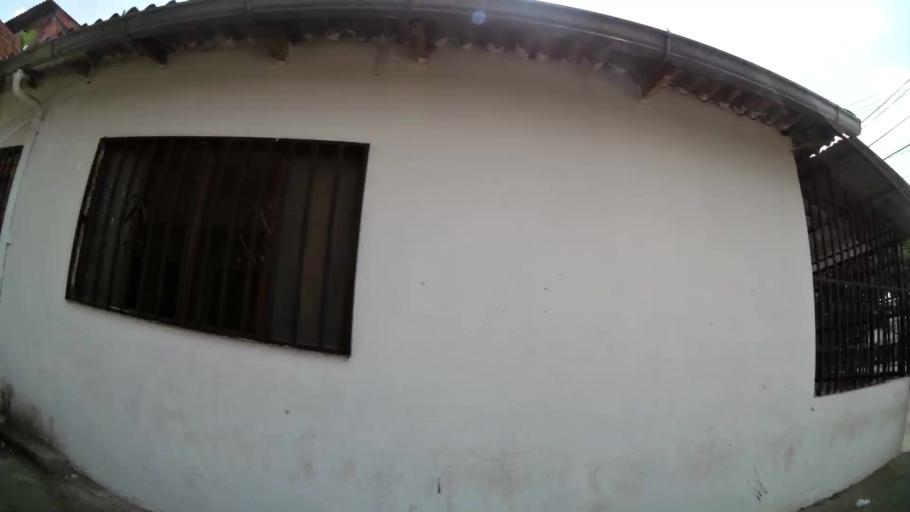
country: CO
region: Valle del Cauca
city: Cali
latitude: 3.4624
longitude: -76.4790
